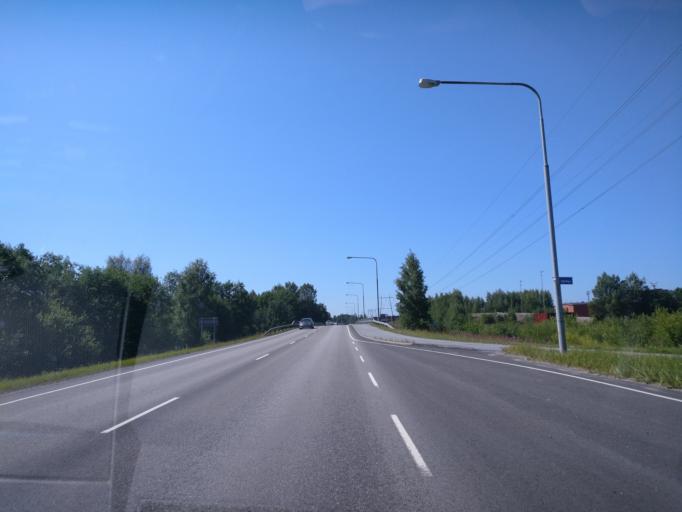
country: FI
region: Satakunta
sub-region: Pori
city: Ulvila
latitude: 61.4563
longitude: 21.8734
